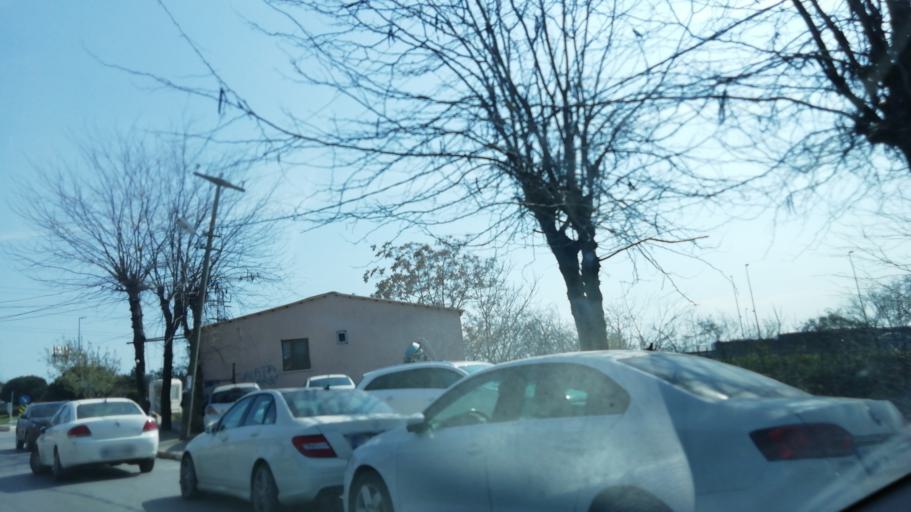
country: TR
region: Istanbul
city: Mahmutbey
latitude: 40.9874
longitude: 28.7739
